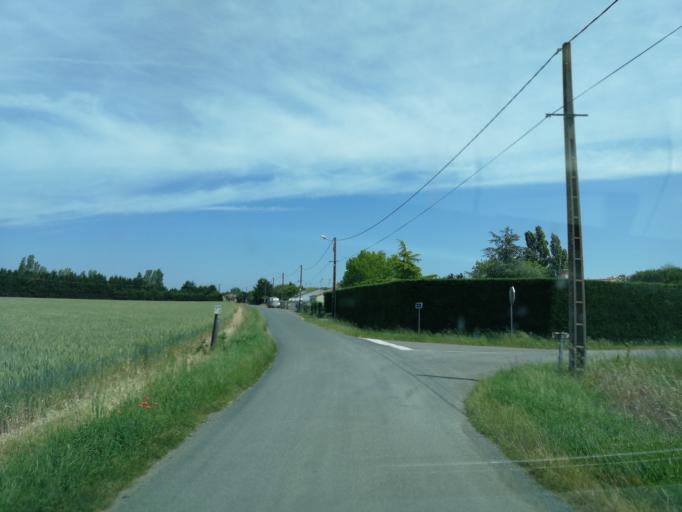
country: FR
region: Pays de la Loire
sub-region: Departement de la Vendee
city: Le Langon
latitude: 46.3805
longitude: -0.9465
